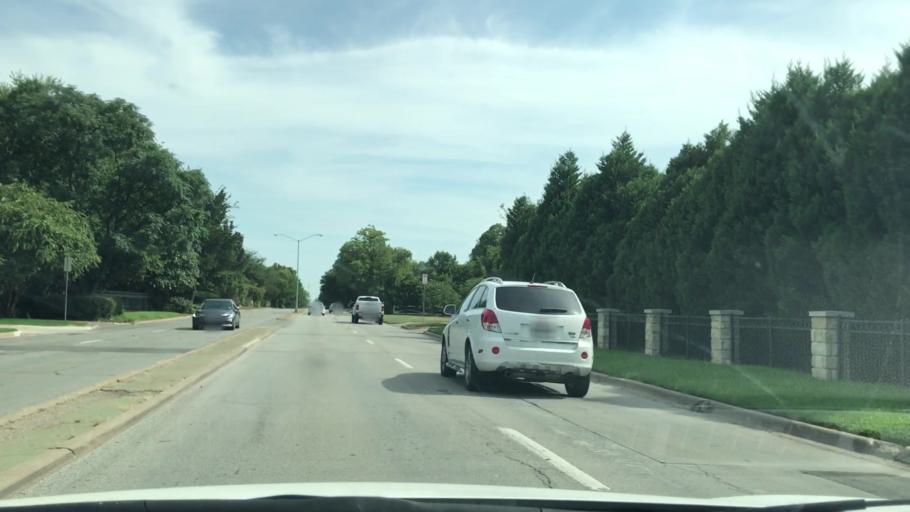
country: US
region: Texas
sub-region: Dallas County
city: University Park
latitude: 32.8597
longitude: -96.8211
